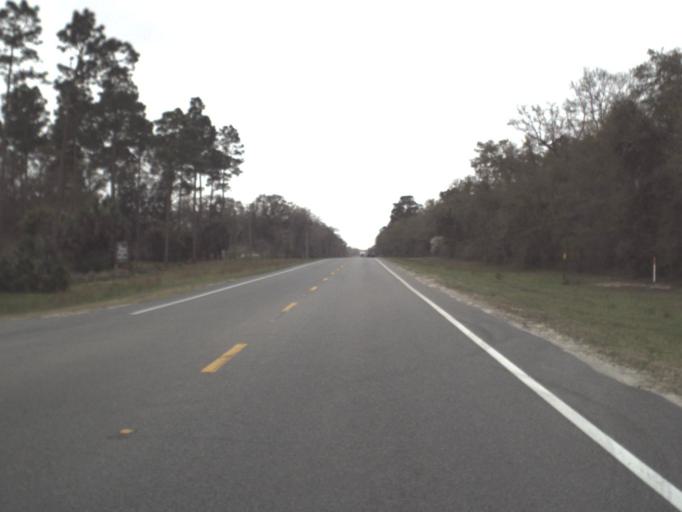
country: US
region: Florida
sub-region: Wakulla County
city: Crawfordville
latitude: 30.1219
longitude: -84.3689
